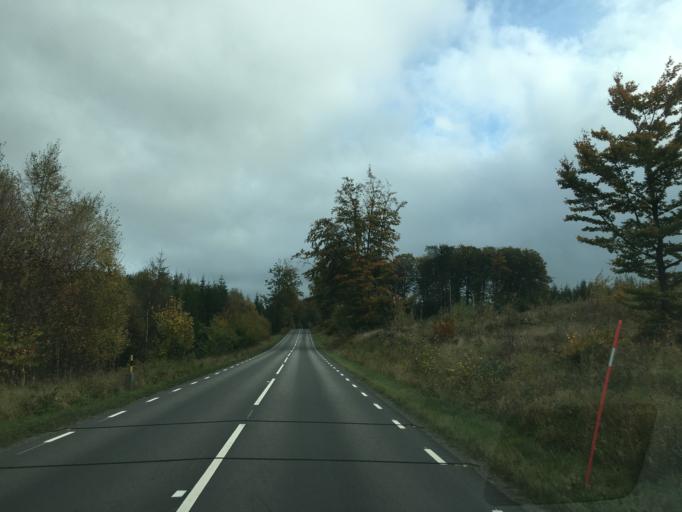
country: SE
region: Skane
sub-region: Tomelilla Kommun
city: Tomelilla
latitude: 55.6358
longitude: 14.0834
